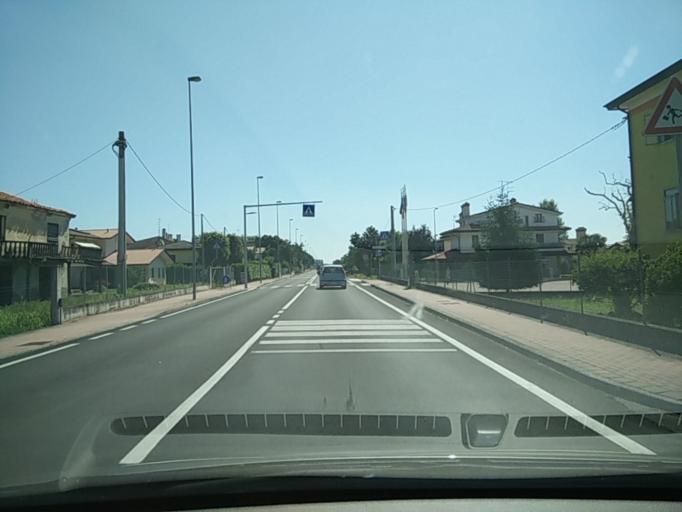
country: IT
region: Veneto
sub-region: Provincia di Venezia
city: Crepaldo
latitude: 45.6365
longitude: 12.6918
